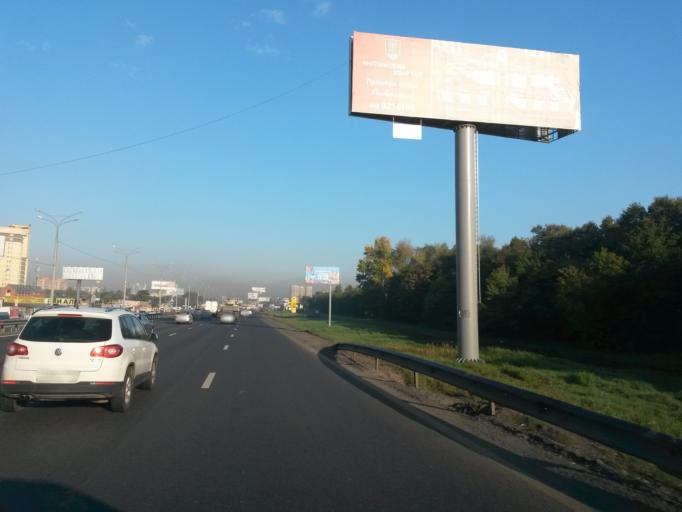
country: RU
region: Moskovskaya
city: Razvilka
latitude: 55.5832
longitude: 37.7455
